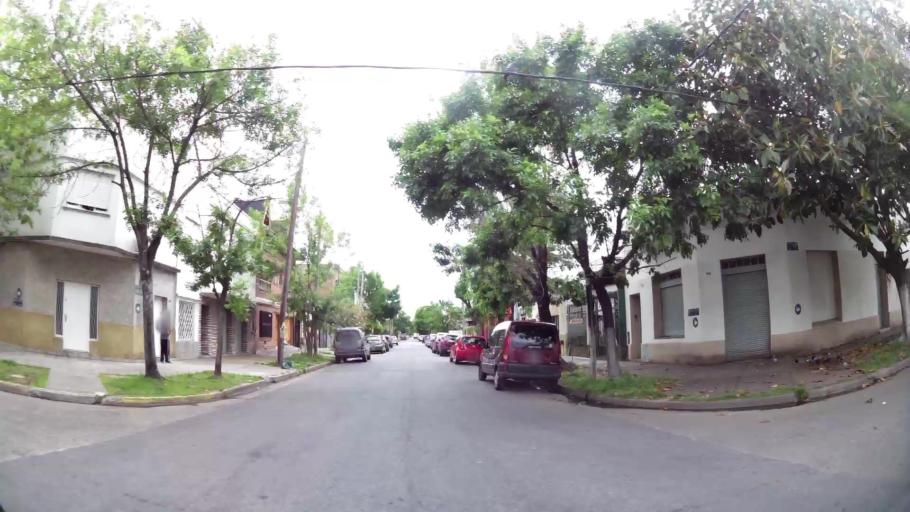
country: AR
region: Buenos Aires
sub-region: Partido de Lanus
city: Lanus
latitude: -34.6867
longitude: -58.3915
